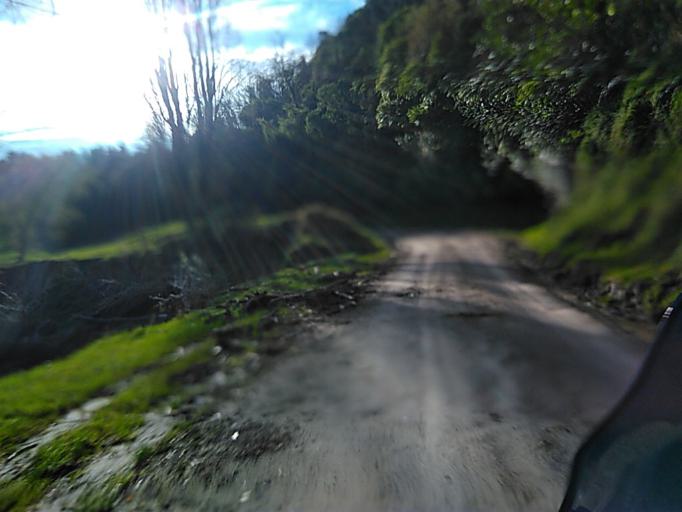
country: NZ
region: Gisborne
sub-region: Gisborne District
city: Gisborne
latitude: -38.5886
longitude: 178.0691
